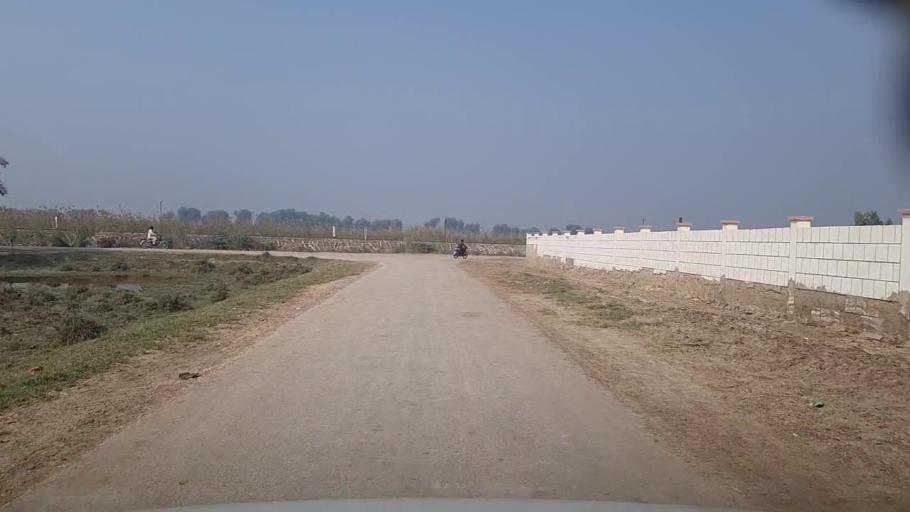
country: PK
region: Sindh
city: Setharja Old
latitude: 27.1927
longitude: 68.4721
